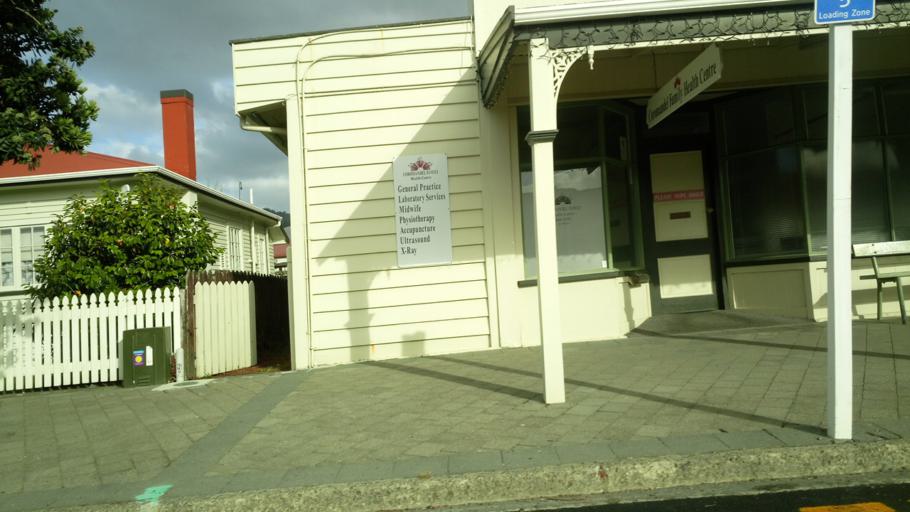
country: NZ
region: Waikato
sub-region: Thames-Coromandel District
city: Coromandel
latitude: -36.7595
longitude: 175.4978
